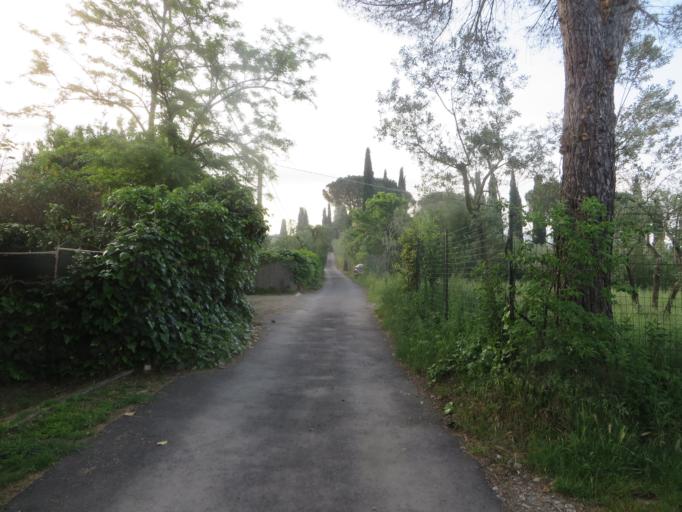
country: IT
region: Tuscany
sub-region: Province of Florence
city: Bagno a Ripoli
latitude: 43.7463
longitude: 11.3182
